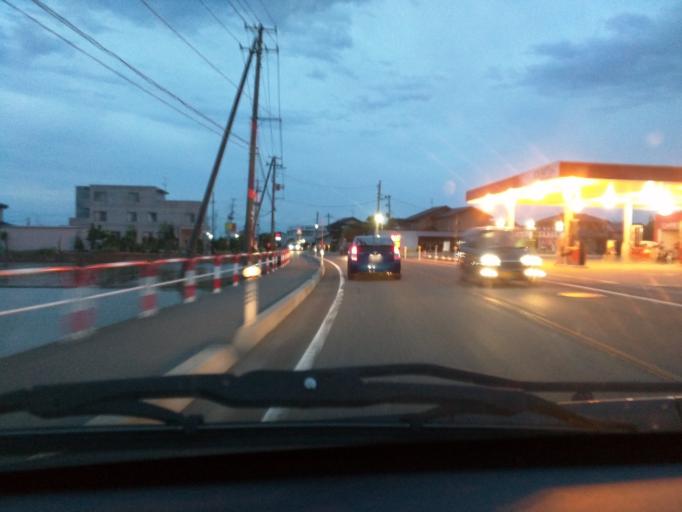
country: JP
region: Niigata
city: Kashiwazaki
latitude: 37.3465
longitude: 138.6108
